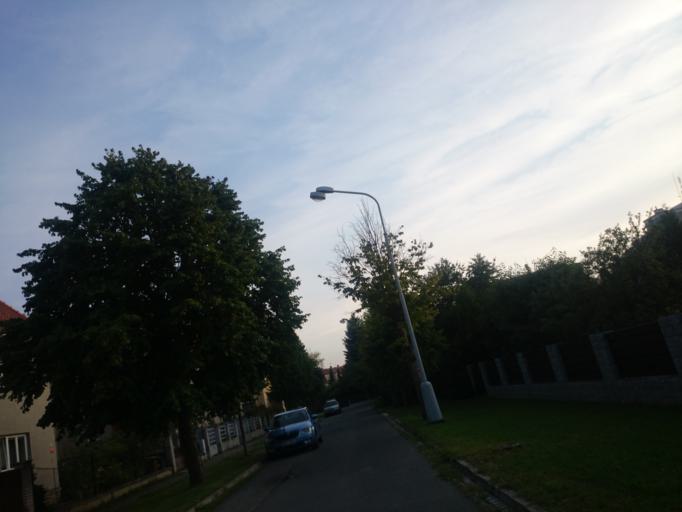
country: CZ
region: Olomoucky
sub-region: Okres Olomouc
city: Olomouc
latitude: 49.6010
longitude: 17.2609
